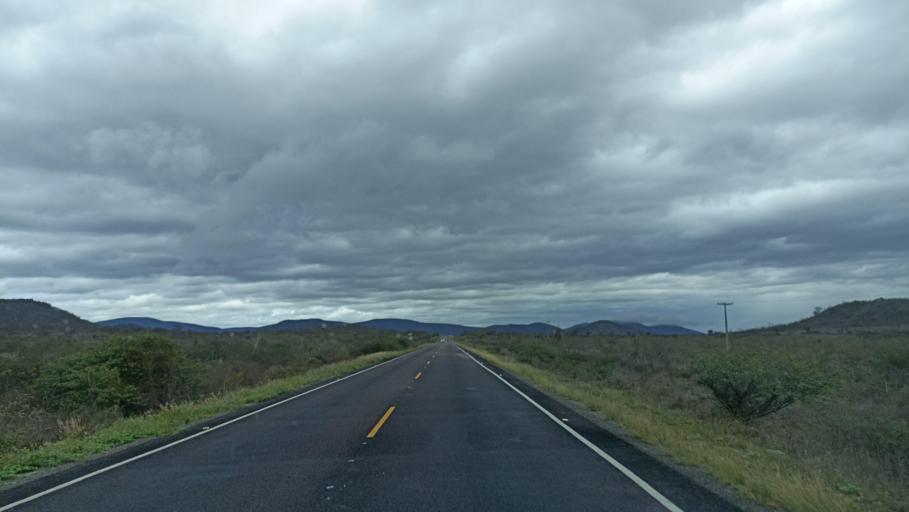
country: BR
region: Bahia
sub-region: Iacu
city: Iacu
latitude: -12.9052
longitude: -40.4052
